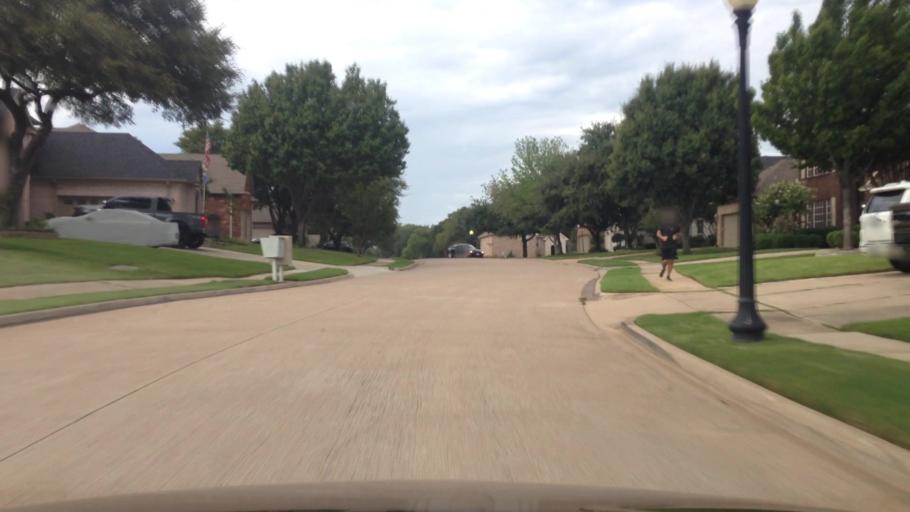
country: US
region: Texas
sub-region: Denton County
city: Flower Mound
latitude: 33.0029
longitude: -97.0460
